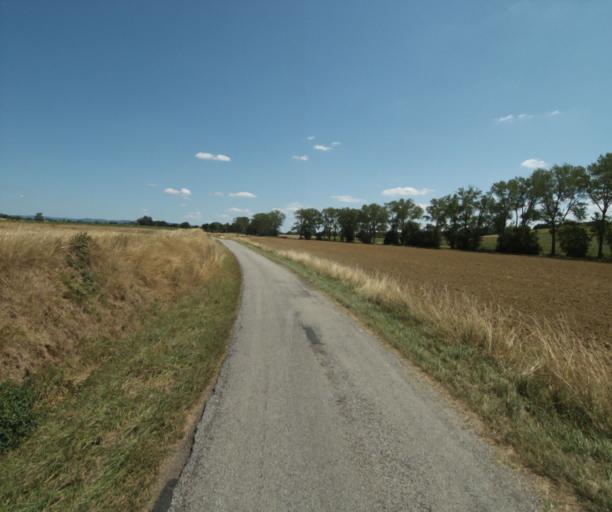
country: FR
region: Midi-Pyrenees
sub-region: Departement de la Haute-Garonne
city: Saint-Felix-Lauragais
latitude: 43.4925
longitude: 1.8695
